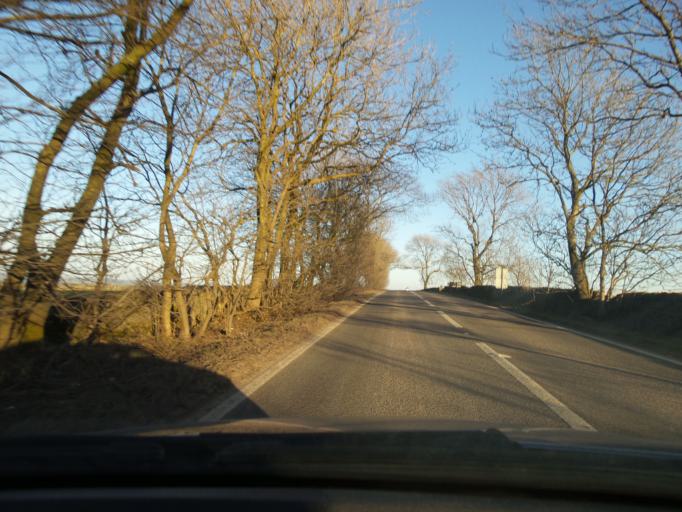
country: GB
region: England
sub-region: Derbyshire
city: Bakewell
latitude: 53.1394
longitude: -1.7449
